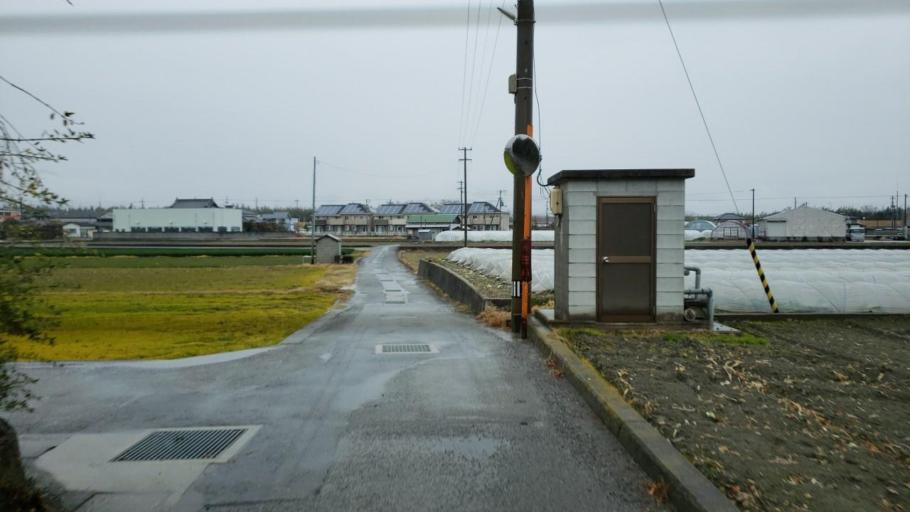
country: JP
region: Tokushima
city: Kamojimacho-jogejima
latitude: 34.0606
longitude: 134.2840
